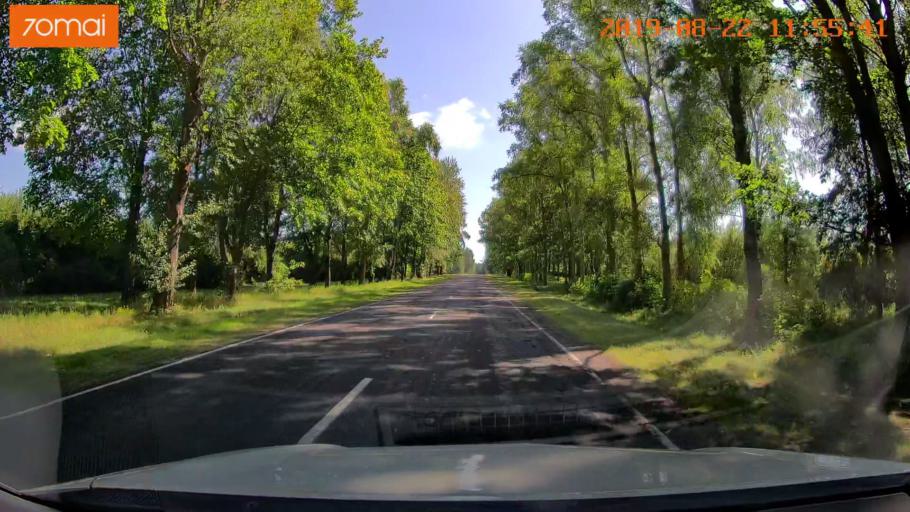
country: BY
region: Minsk
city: Prawdzinski
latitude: 53.4307
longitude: 27.5535
